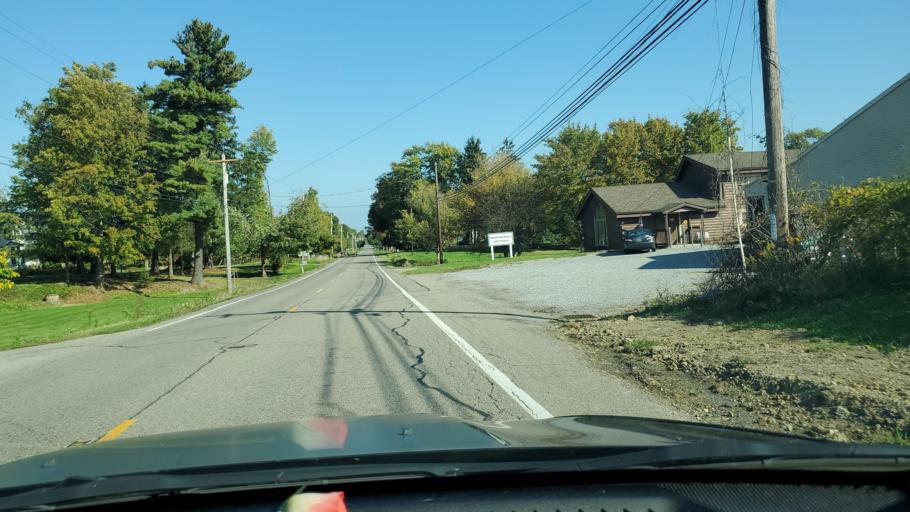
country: US
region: Ohio
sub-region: Trumbull County
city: Brookfield Center
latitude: 41.3505
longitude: -80.5694
